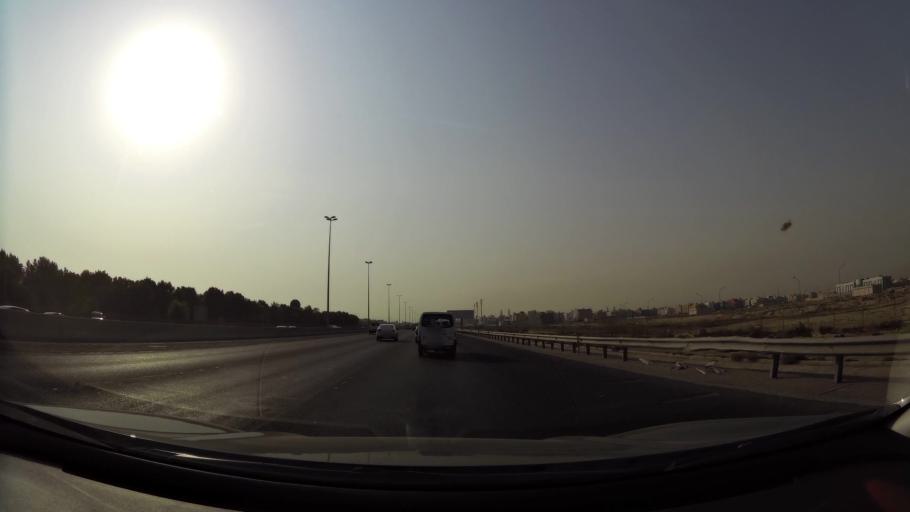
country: KW
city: Al Funaytis
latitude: 29.2444
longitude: 48.0930
